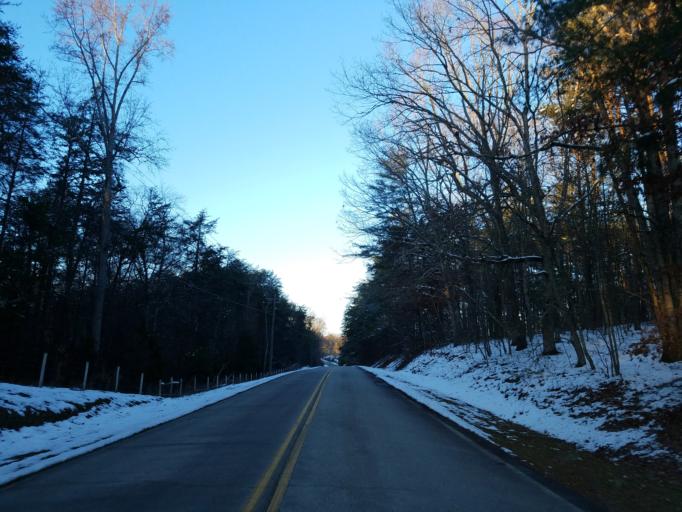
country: US
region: Georgia
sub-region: Dawson County
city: Dawsonville
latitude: 34.4318
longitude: -84.1933
